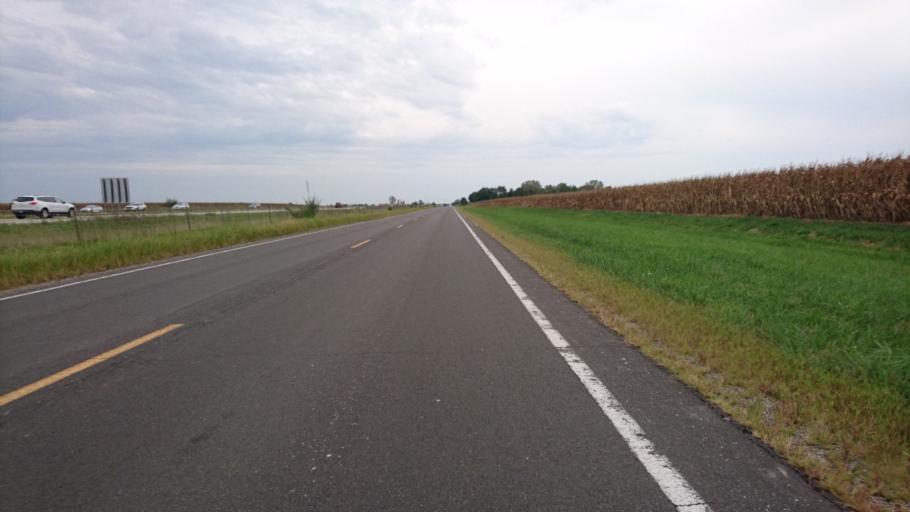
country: US
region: Illinois
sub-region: Sangamon County
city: Chatham
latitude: 39.6639
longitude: -89.6480
